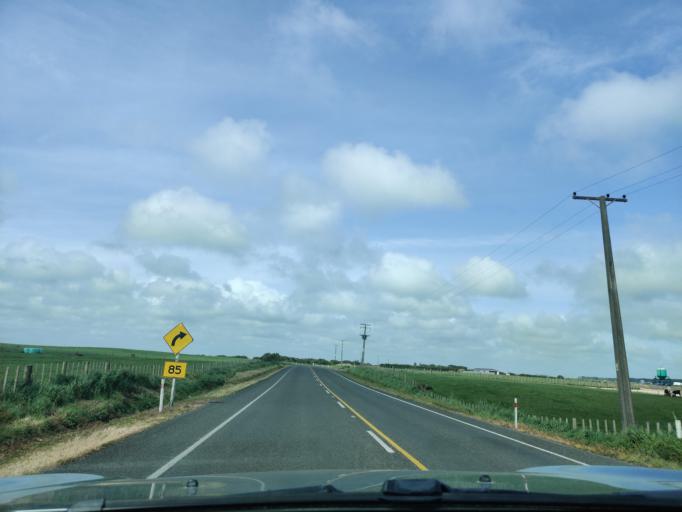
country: NZ
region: Taranaki
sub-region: South Taranaki District
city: Patea
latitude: -39.7669
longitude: 174.5543
